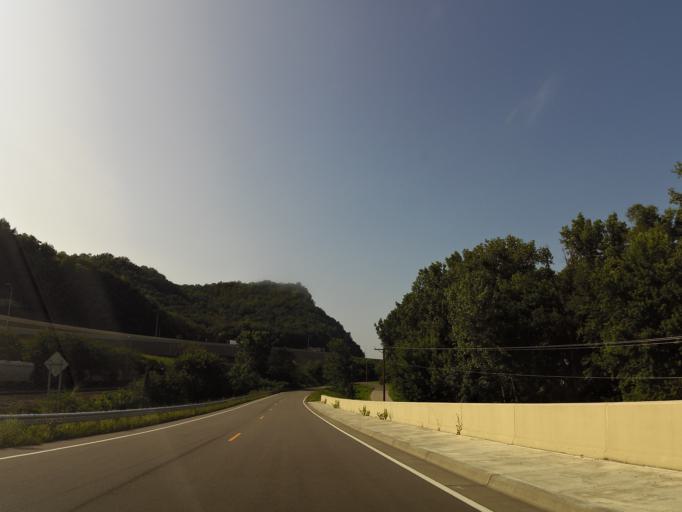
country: US
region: Minnesota
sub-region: Houston County
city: La Crescent
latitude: 43.8609
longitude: -91.3080
